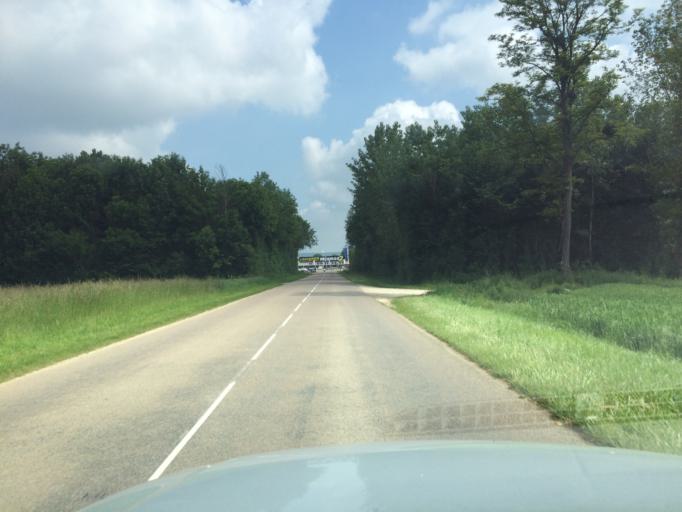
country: FR
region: Bourgogne
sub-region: Departement de l'Yonne
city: Laroche-Saint-Cydroine
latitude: 47.9545
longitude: 3.4477
